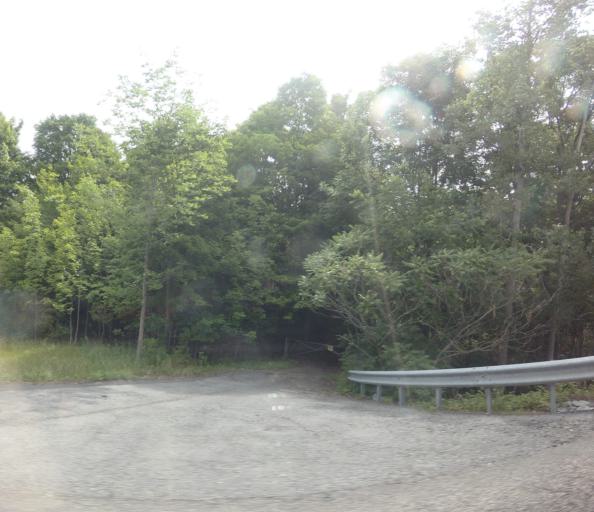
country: US
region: New York
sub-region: Onondaga County
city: Camillus
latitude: 43.0373
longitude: -76.3036
